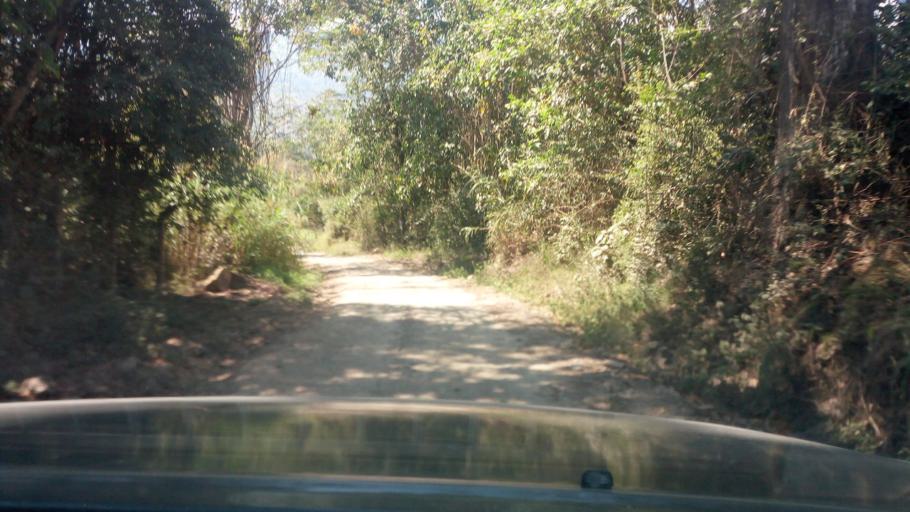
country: CO
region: Boyaca
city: Somondoco
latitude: 4.9838
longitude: -73.4452
